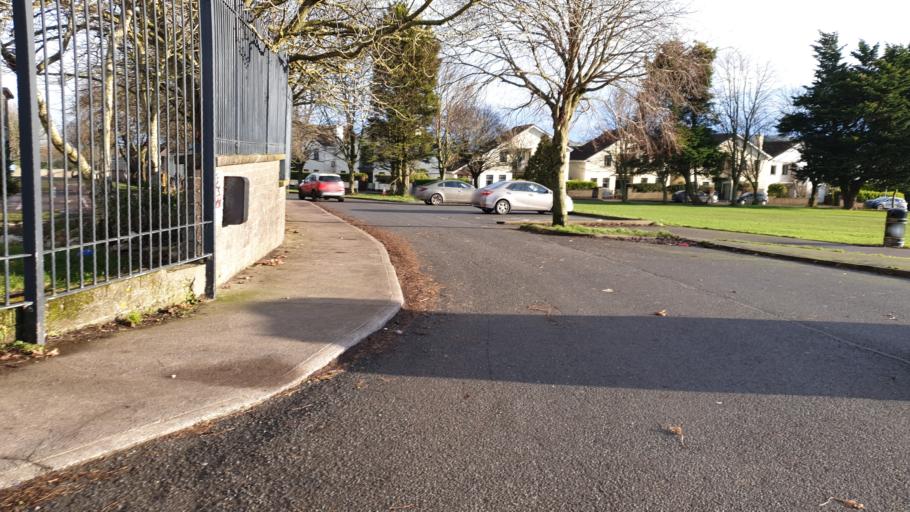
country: IE
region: Munster
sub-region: County Cork
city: Cork
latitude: 51.8888
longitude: -8.4290
